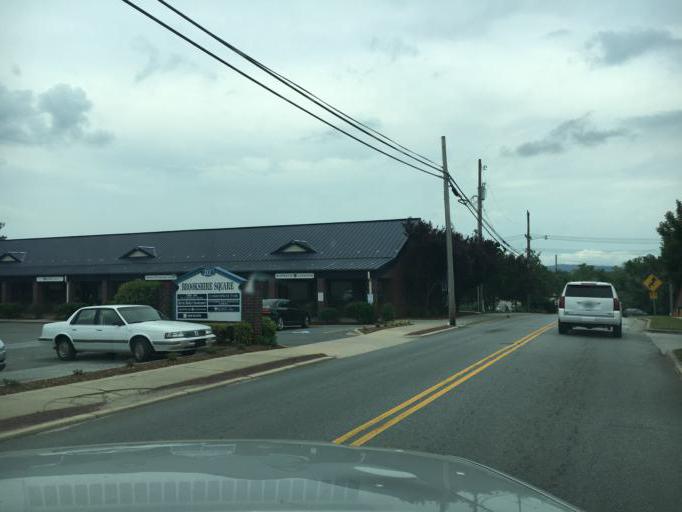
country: US
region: North Carolina
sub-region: Henderson County
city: Hendersonville
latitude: 35.3137
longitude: -82.4571
